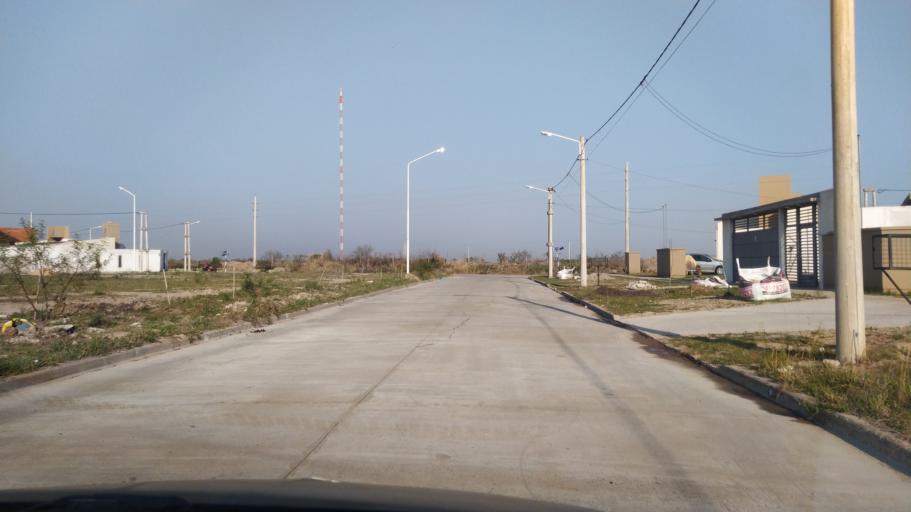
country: AR
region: Corrientes
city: Corrientes
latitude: -27.5267
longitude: -58.8074
